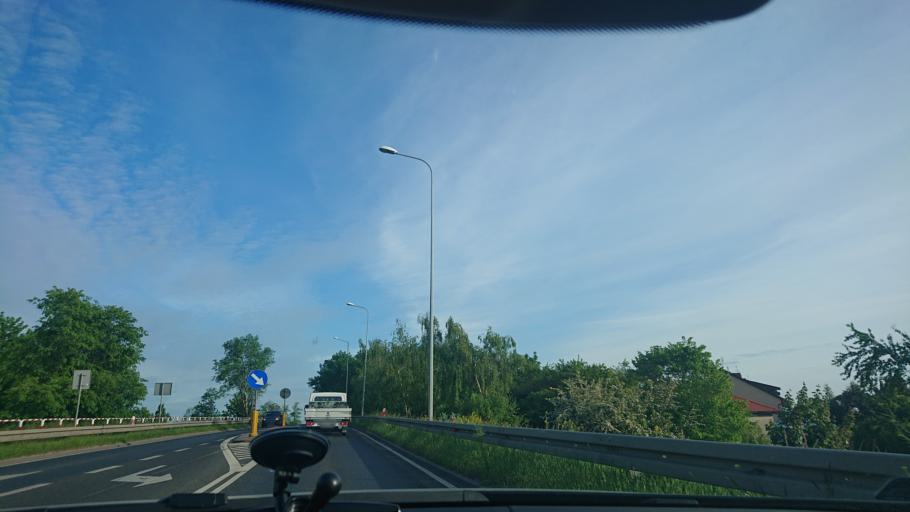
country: PL
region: Greater Poland Voivodeship
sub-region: Powiat gnieznienski
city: Gniezno
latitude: 52.5286
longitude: 17.5839
